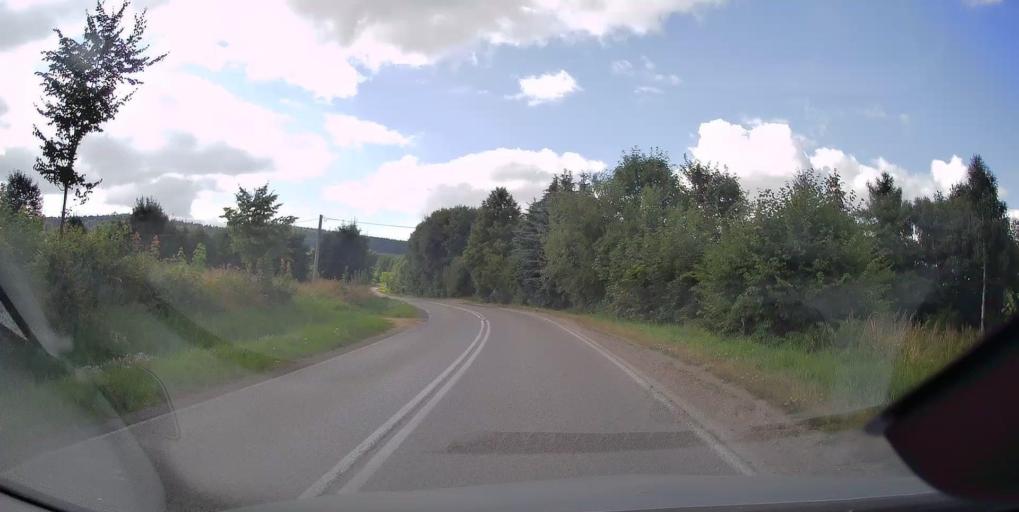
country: PL
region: Swietokrzyskie
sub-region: Powiat kielecki
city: Nowa Slupia
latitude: 50.8471
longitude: 21.0881
